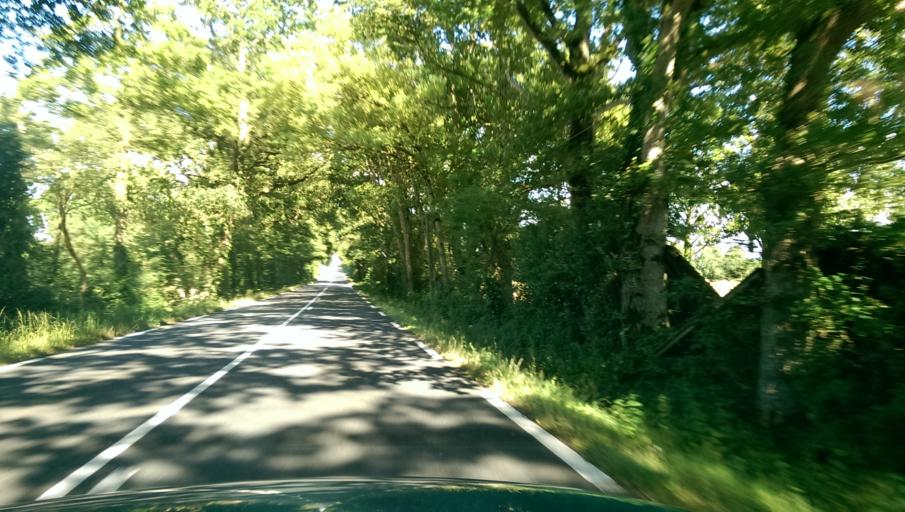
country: FR
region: Pays de la Loire
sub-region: Departement de la Loire-Atlantique
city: Touvois
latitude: 46.8825
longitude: -1.6820
